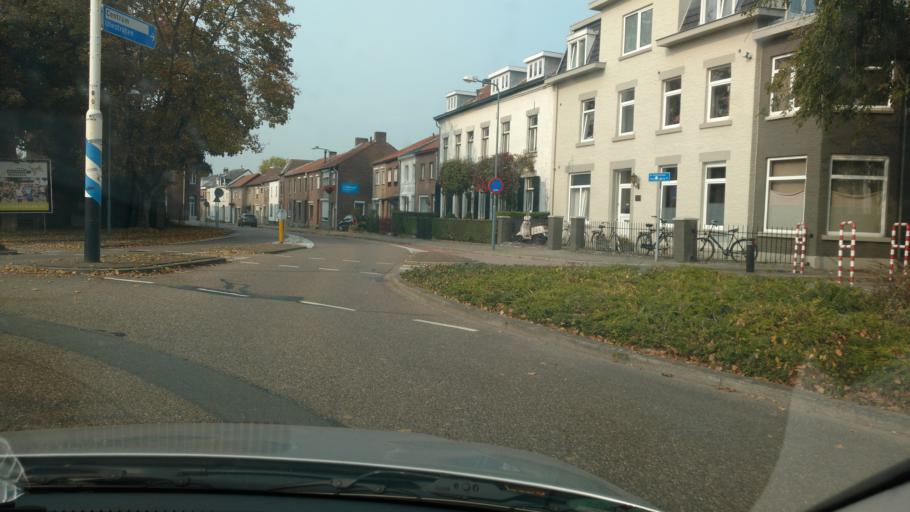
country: NL
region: Limburg
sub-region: Gemeente Meerssen
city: Meerssen
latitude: 50.8838
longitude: 5.7606
